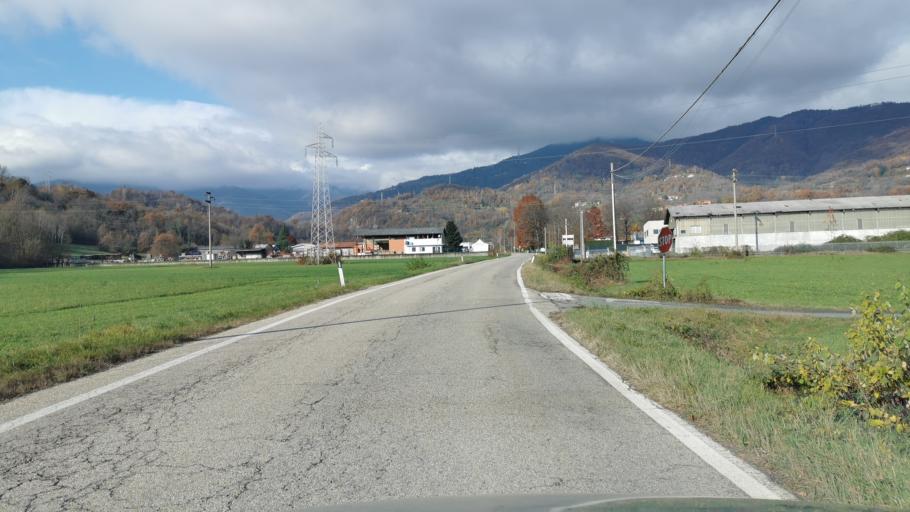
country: IT
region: Piedmont
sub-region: Provincia di Torino
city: Rocca Canavese
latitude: 45.3041
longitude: 7.5851
